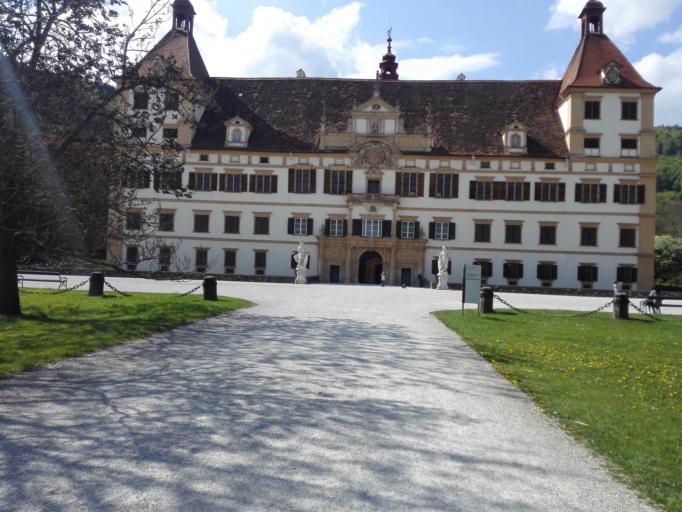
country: AT
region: Styria
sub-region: Graz Stadt
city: Wetzelsdorf
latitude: 47.0735
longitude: 15.3926
